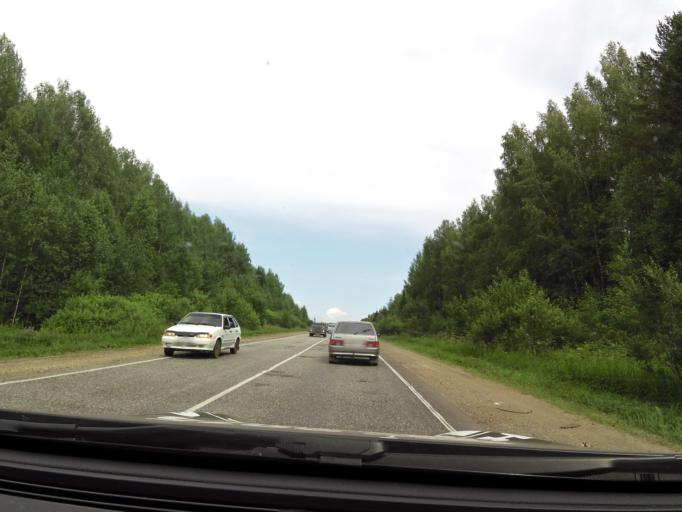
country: RU
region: Kirov
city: Vakhrushi
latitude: 58.6564
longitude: 49.9043
